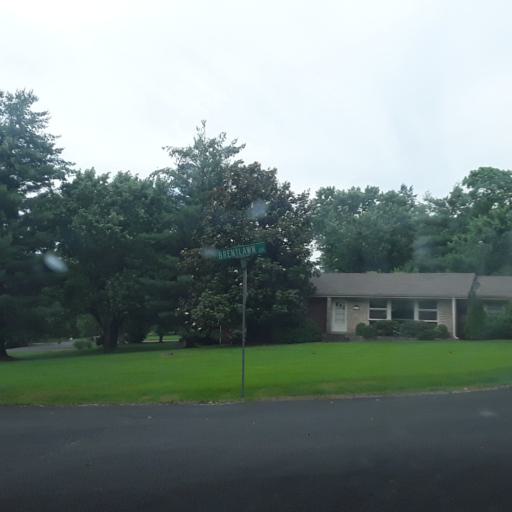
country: US
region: Tennessee
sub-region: Davidson County
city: Oak Hill
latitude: 36.0639
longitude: -86.7531
